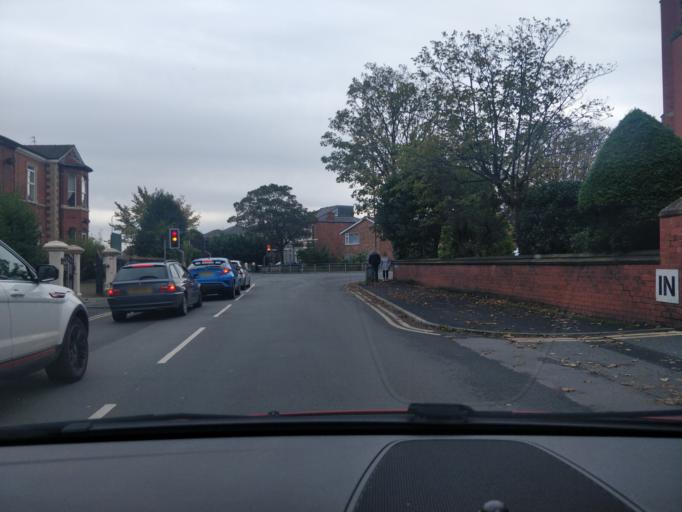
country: GB
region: England
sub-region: Sefton
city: Southport
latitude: 53.6478
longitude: -2.9955
